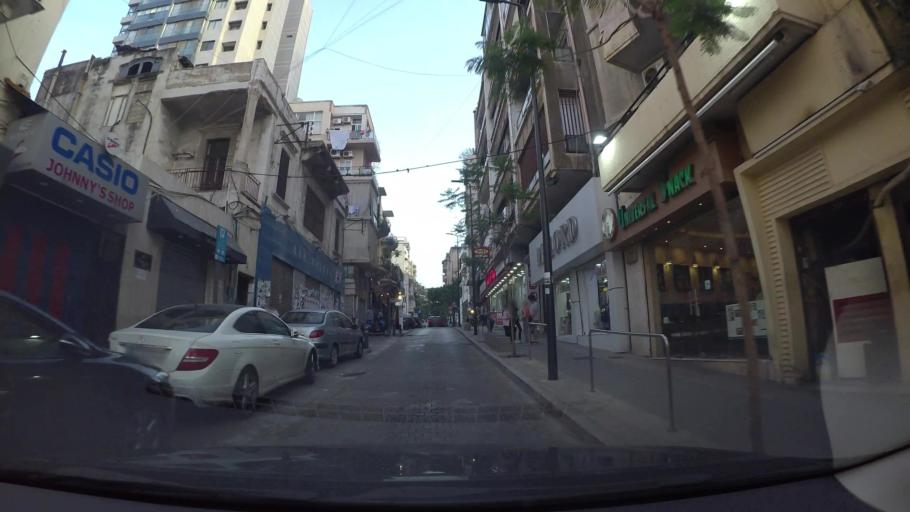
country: LB
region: Beyrouth
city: Ra's Bayrut
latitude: 33.8993
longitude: 35.4817
